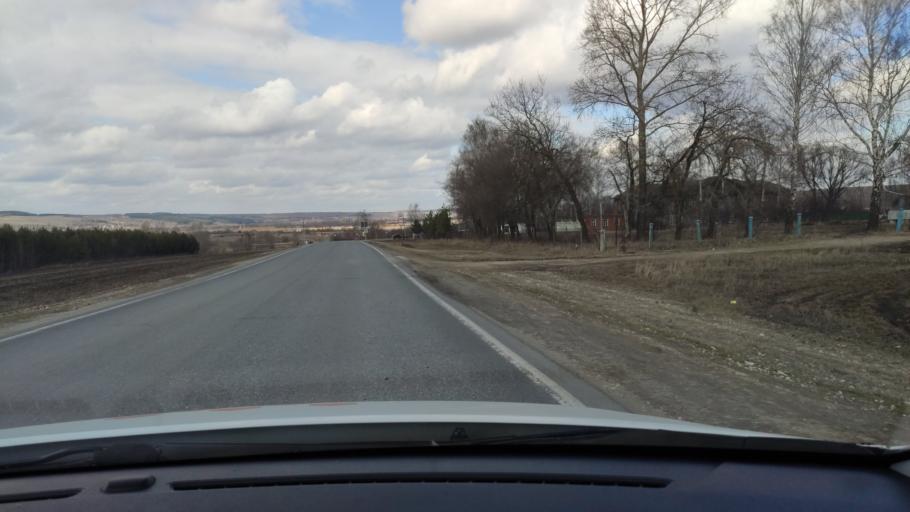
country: RU
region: Tatarstan
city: Vysokaya Gora
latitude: 56.1941
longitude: 49.2078
